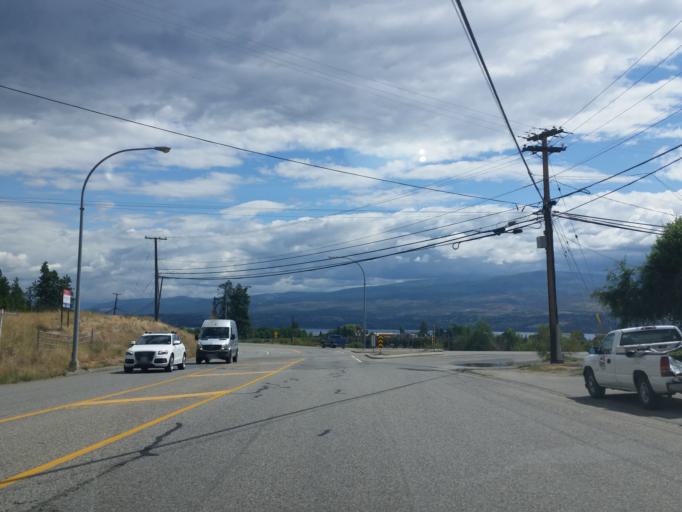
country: CA
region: British Columbia
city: West Kelowna
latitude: 49.8311
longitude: -119.5897
